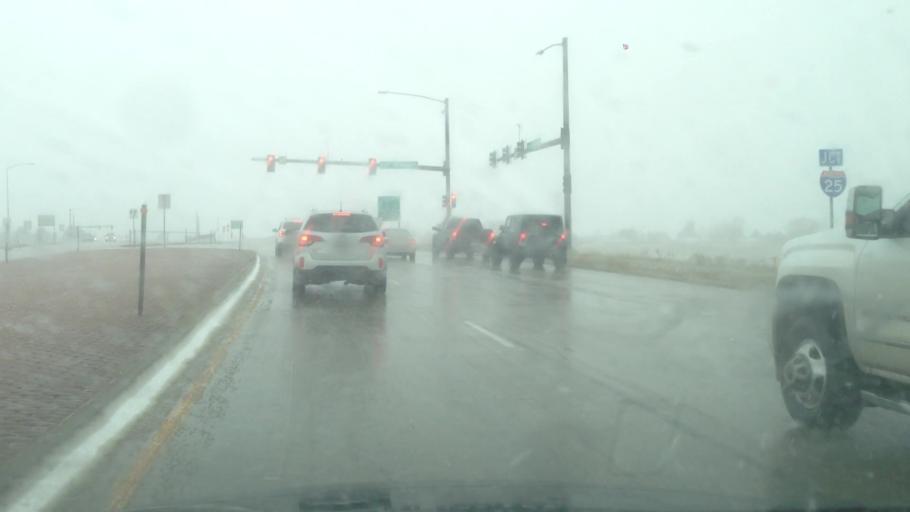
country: US
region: Colorado
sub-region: Park County
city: Castle Pines North
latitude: 39.4719
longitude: -104.8695
